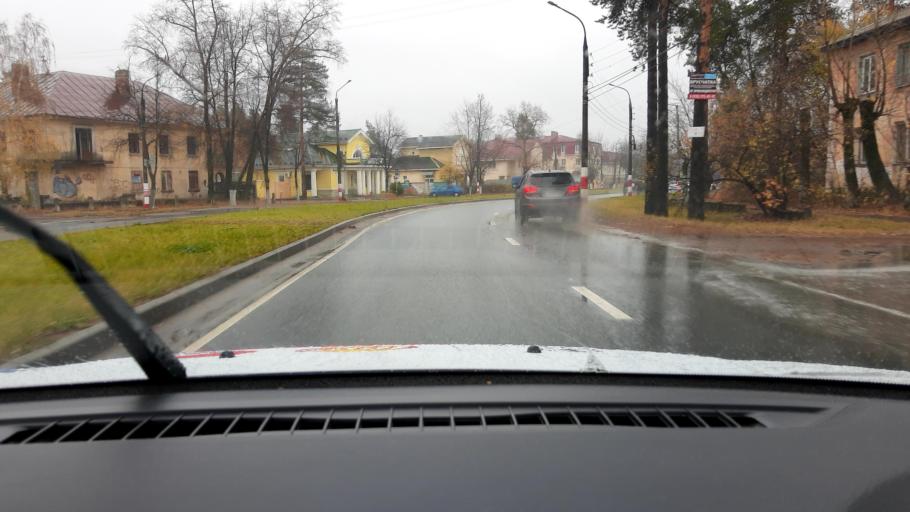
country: RU
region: Nizjnij Novgorod
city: Dzerzhinsk
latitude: 56.2462
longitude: 43.4312
